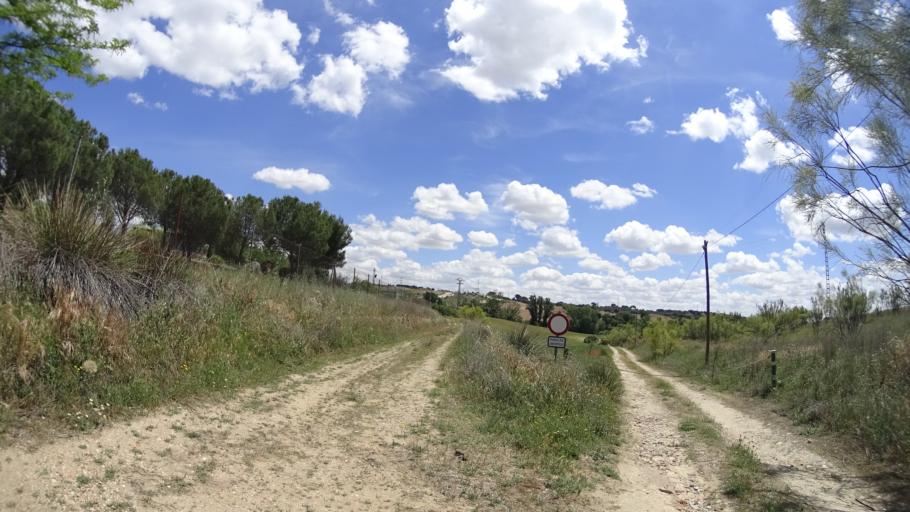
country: ES
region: Madrid
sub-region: Provincia de Madrid
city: Boadilla del Monte
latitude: 40.4120
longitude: -3.9212
